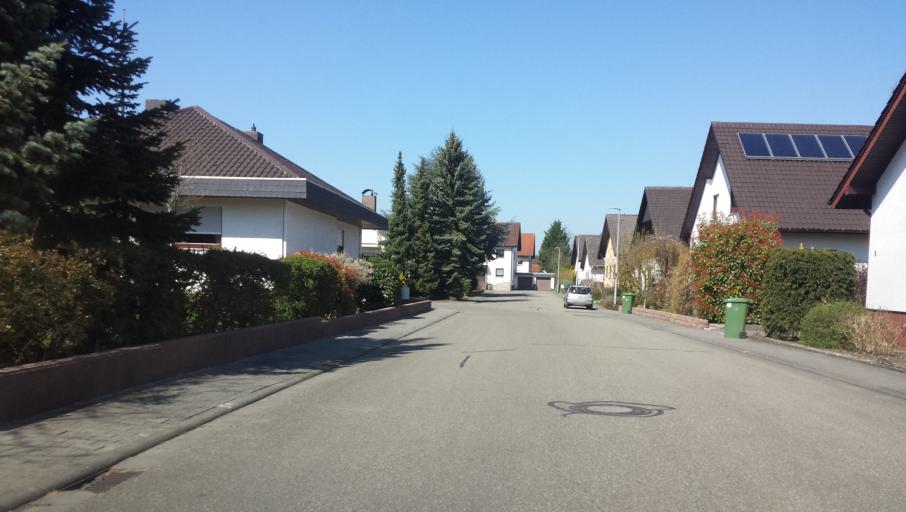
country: DE
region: Hesse
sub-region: Regierungsbezirk Darmstadt
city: Biblis
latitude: 49.6870
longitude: 8.4447
